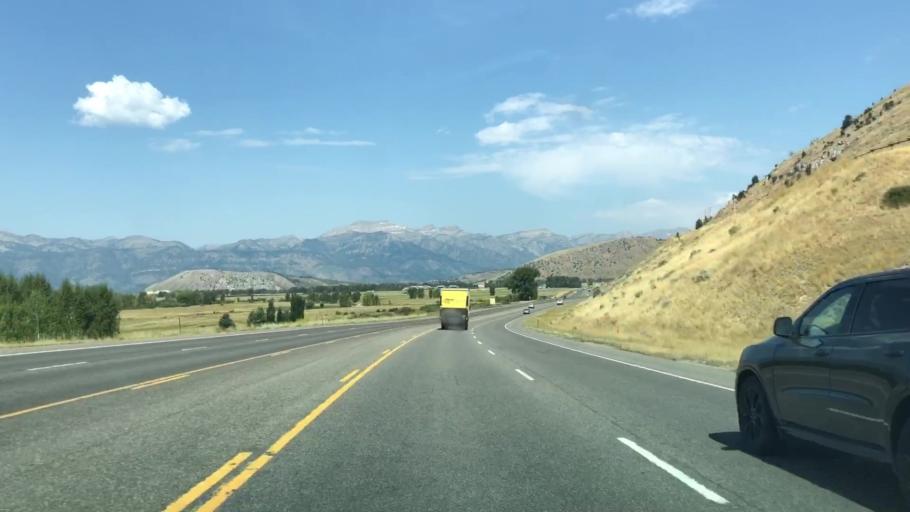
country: US
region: Wyoming
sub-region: Teton County
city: South Park
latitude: 43.4353
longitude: -110.7853
